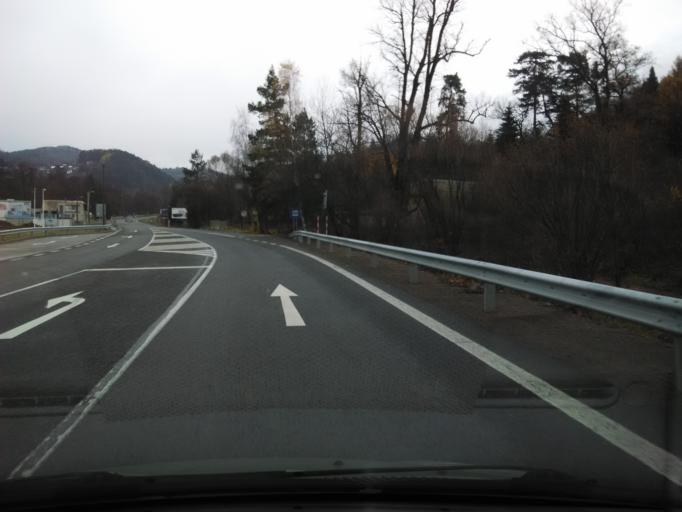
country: SK
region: Banskobystricky
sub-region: Okres Ziar nad Hronom
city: Kremnica
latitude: 48.6857
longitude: 18.9184
